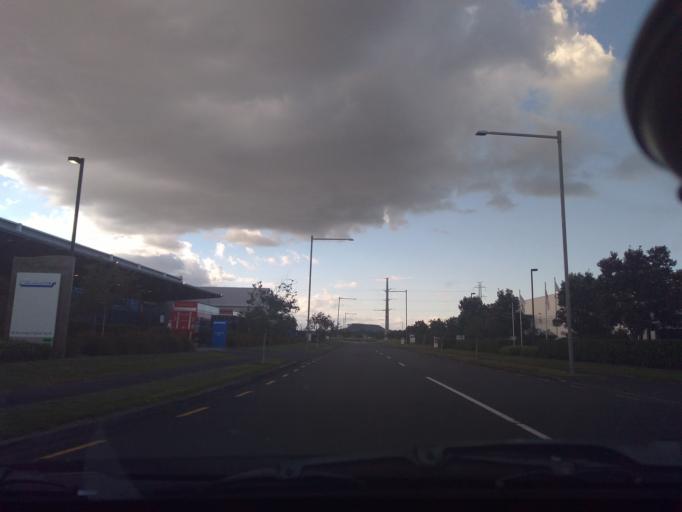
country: NZ
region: Auckland
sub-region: Auckland
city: Tamaki
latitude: -36.9318
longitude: 174.8755
